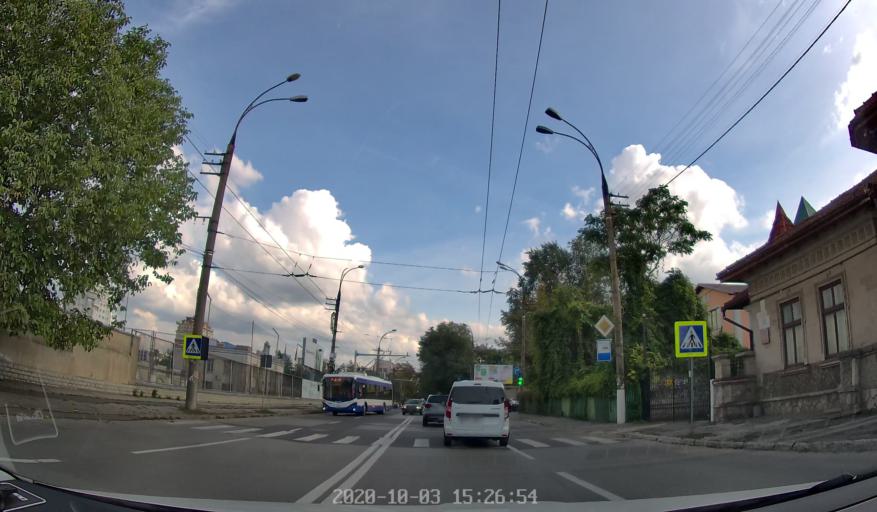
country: MD
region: Chisinau
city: Chisinau
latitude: 47.0266
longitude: 28.8177
